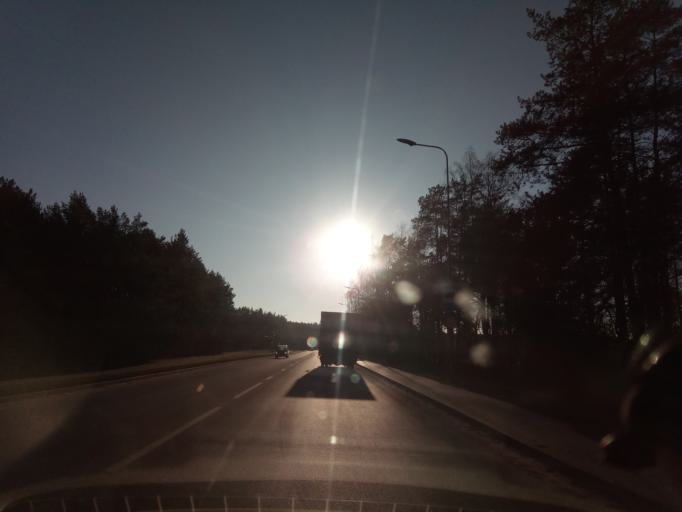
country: LT
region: Alytaus apskritis
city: Druskininkai
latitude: 54.0129
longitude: 23.9944
